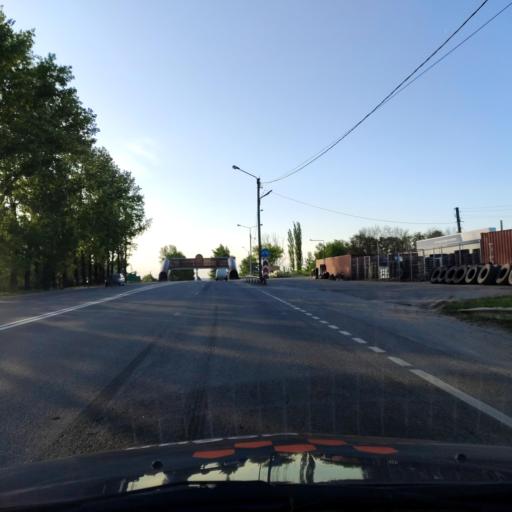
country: RU
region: Lipetsk
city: Yelets
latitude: 52.5953
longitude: 38.4810
